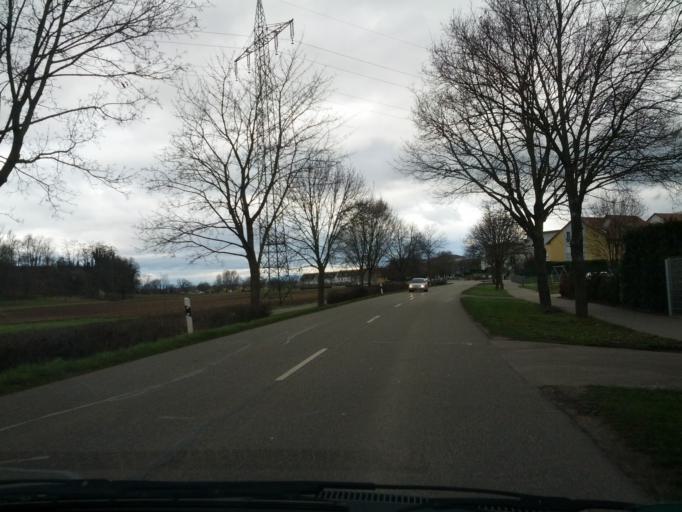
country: DE
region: Baden-Wuerttemberg
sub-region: Freiburg Region
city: Unterkrozingen
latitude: 47.9216
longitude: 7.6850
